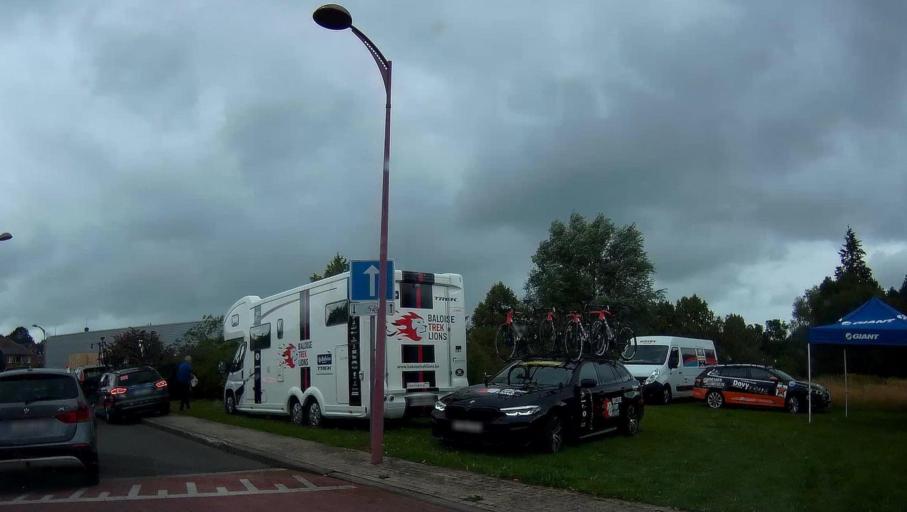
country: BE
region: Wallonia
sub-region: Province de Namur
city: Couvin
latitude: 50.0547
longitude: 4.4953
